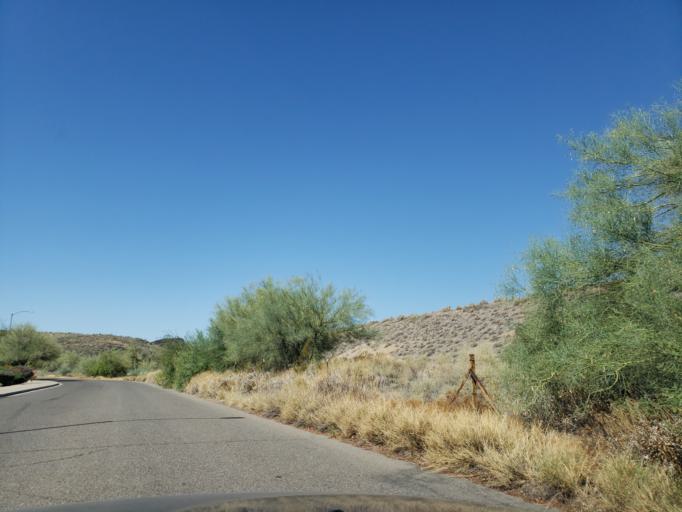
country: US
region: Arizona
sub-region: Maricopa County
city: Peoria
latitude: 33.6829
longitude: -112.1424
